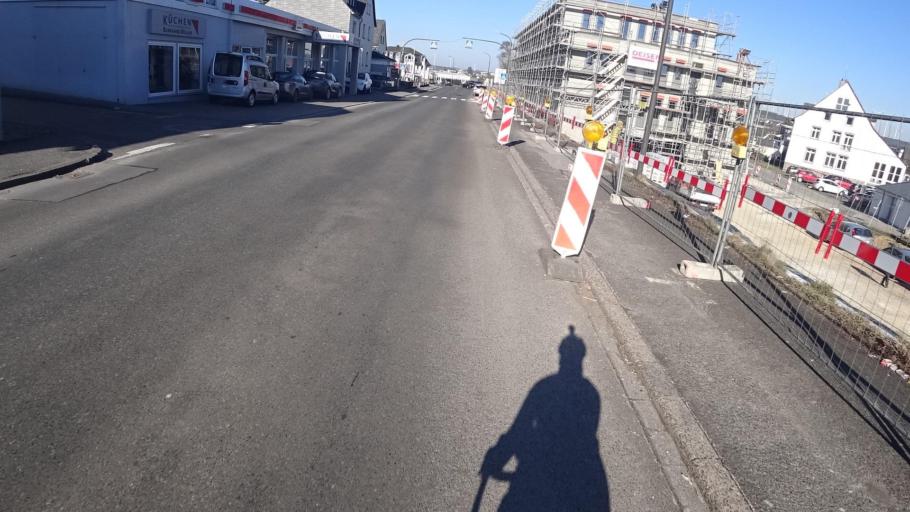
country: DE
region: Rheinland-Pfalz
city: Simmern
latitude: 49.9837
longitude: 7.5339
